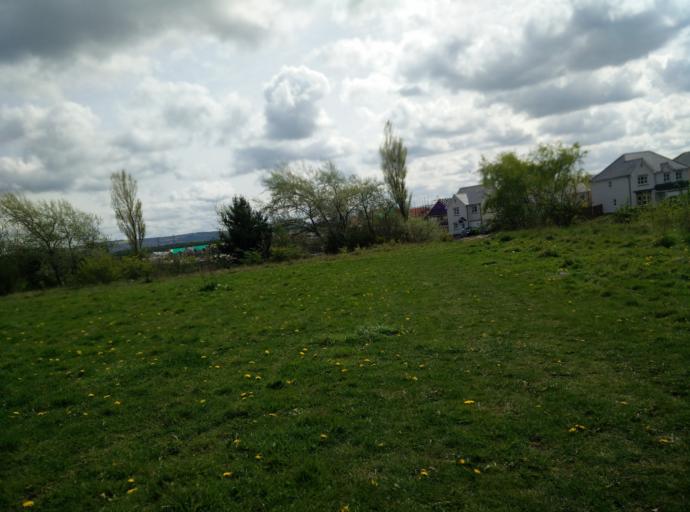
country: GB
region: Scotland
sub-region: Midlothian
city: Dalkeith
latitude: 55.9147
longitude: -3.1025
